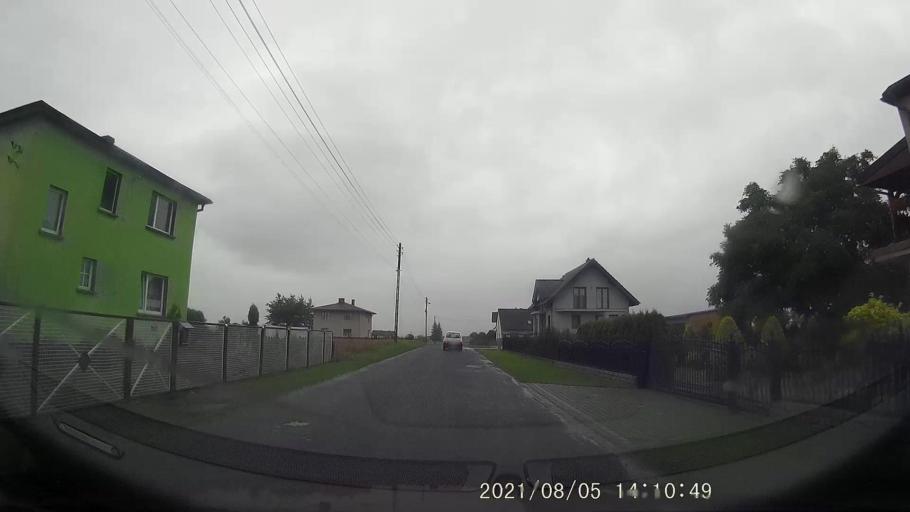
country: PL
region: Opole Voivodeship
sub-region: Powiat krapkowicki
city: Strzeleczki
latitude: 50.4719
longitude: 17.7856
